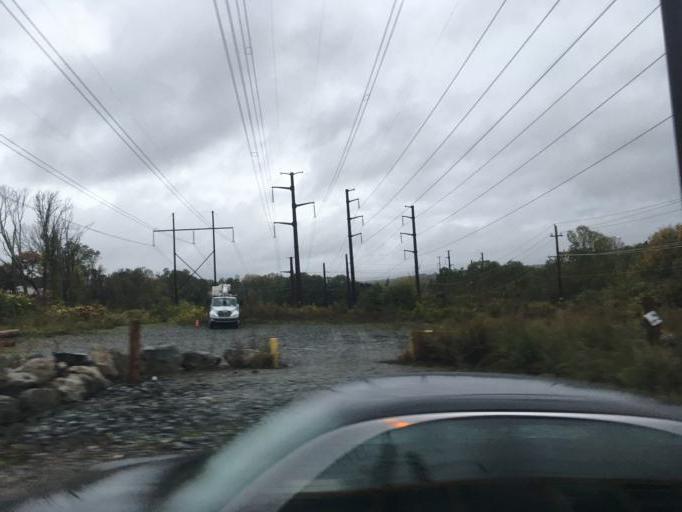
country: US
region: Rhode Island
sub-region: Kent County
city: West Warwick
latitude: 41.7106
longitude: -71.5058
